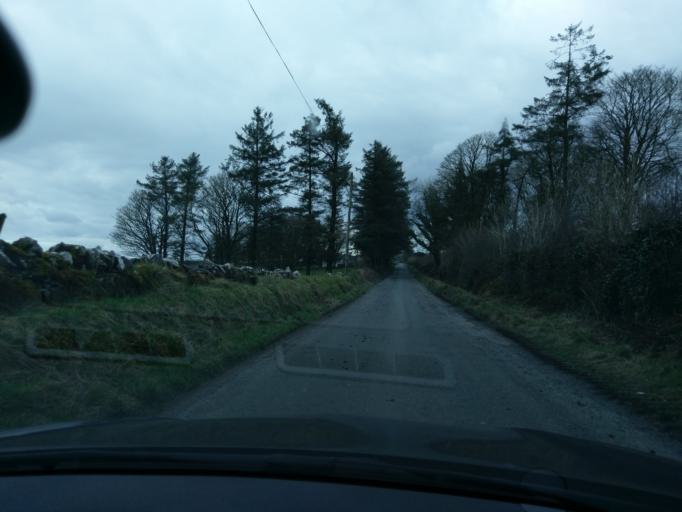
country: IE
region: Connaught
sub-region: County Galway
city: Athenry
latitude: 53.4572
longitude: -8.5824
